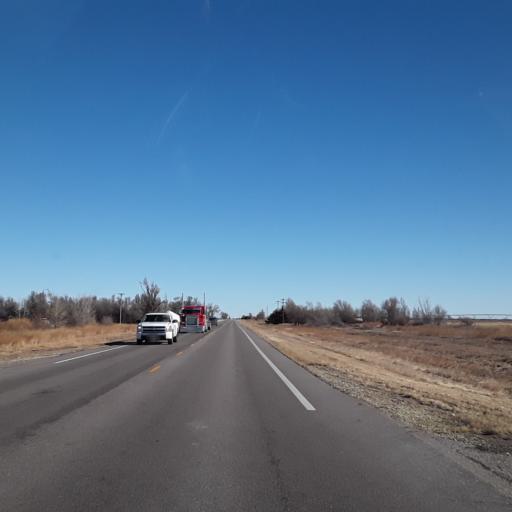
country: US
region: Kansas
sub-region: Pawnee County
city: Larned
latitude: 38.1147
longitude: -99.1868
